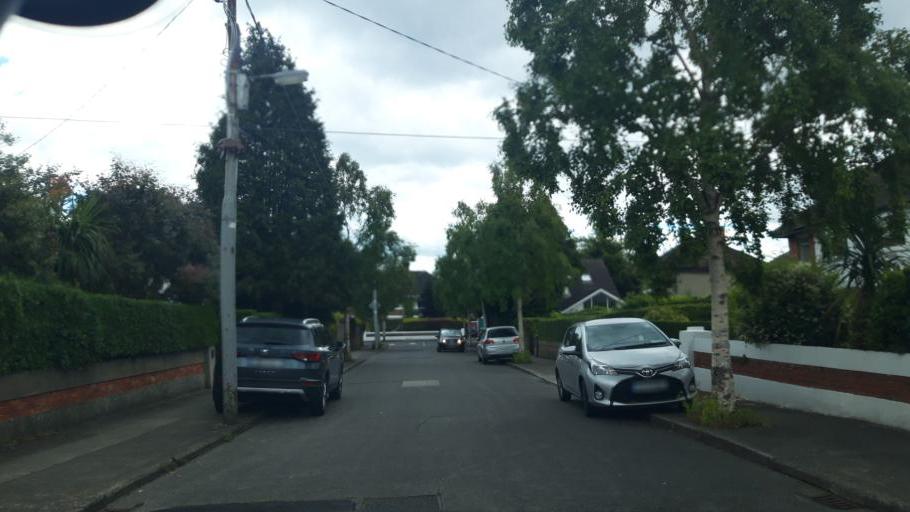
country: IE
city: Killester
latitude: 53.3671
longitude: -6.1992
